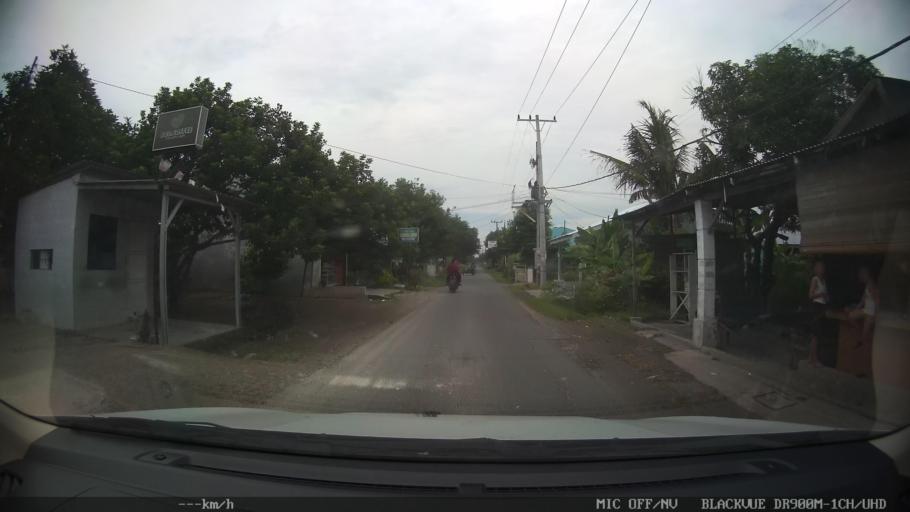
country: ID
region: North Sumatra
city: Sunggal
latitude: 3.6242
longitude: 98.5904
